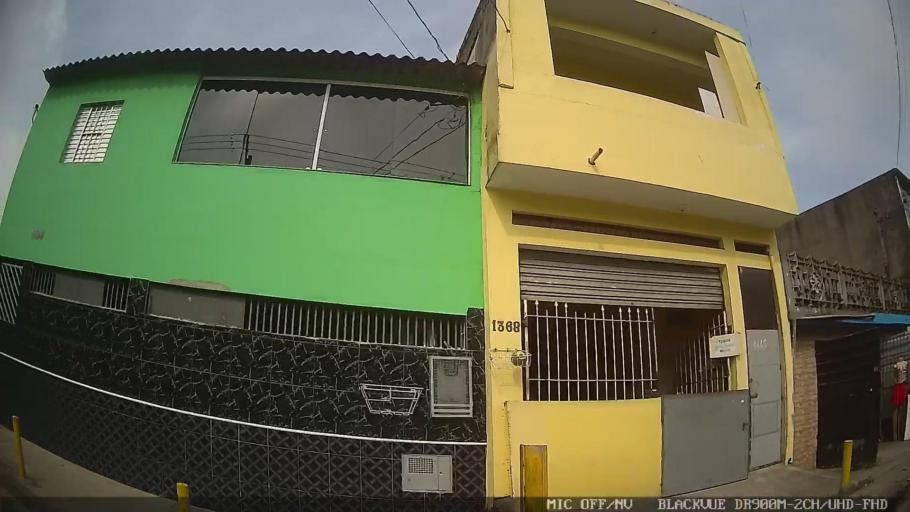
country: BR
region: Sao Paulo
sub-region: Itaquaquecetuba
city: Itaquaquecetuba
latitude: -23.4991
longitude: -46.3677
